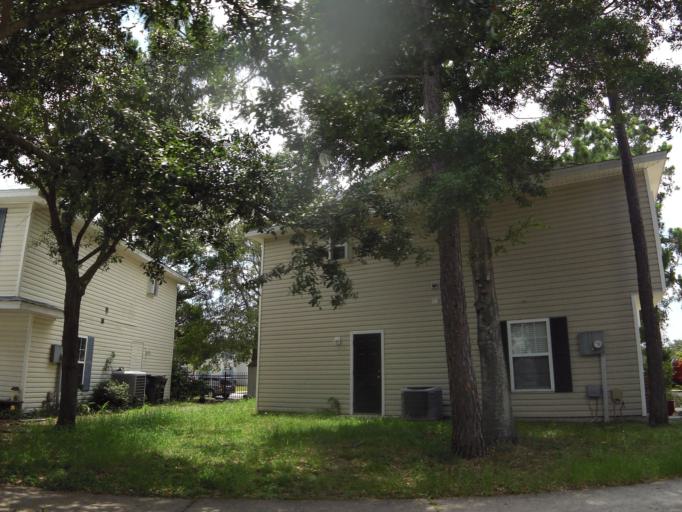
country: US
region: Florida
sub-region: Duval County
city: Atlantic Beach
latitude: 30.3273
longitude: -81.4161
